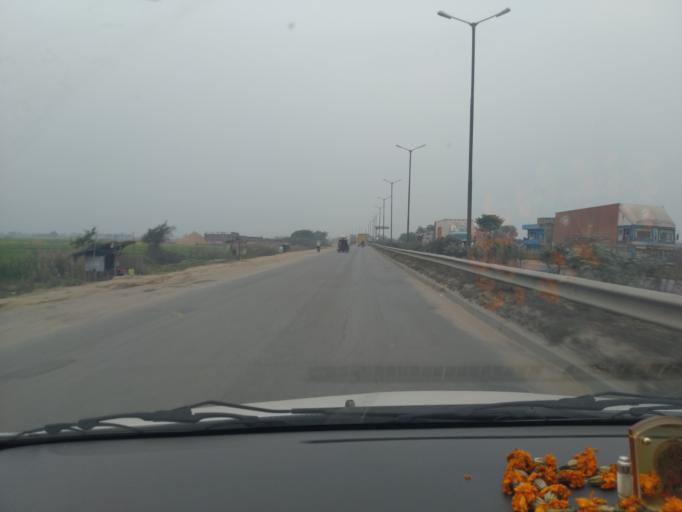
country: IN
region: Bihar
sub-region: Rohtas
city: Dehri
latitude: 24.9617
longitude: 83.9418
